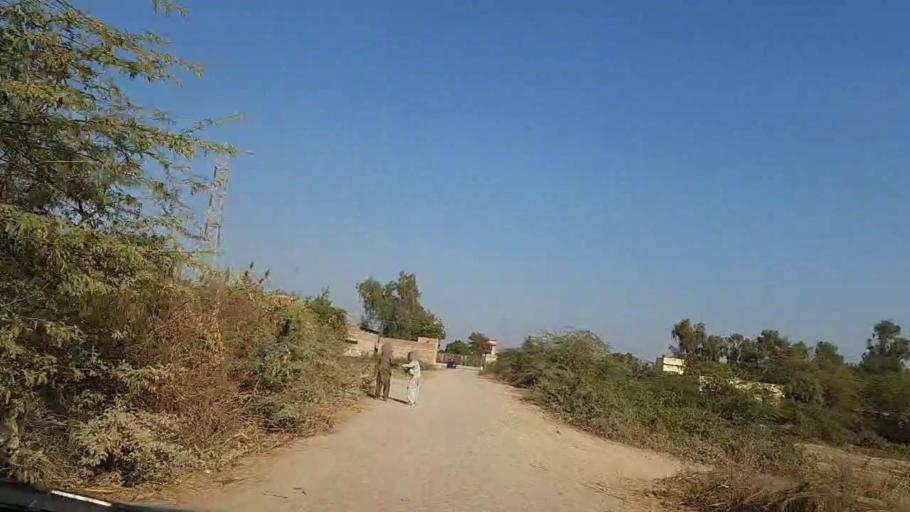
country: PK
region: Sindh
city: Sakrand
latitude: 26.0211
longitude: 68.3456
